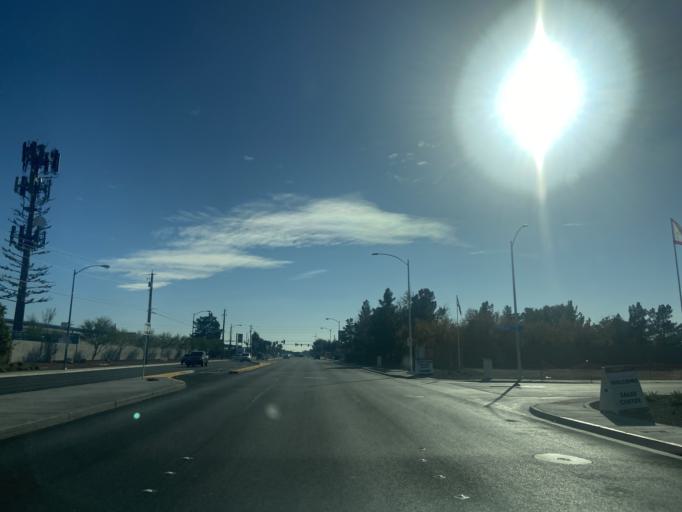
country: US
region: Nevada
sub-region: Clark County
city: North Las Vegas
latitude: 36.2418
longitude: -115.1802
